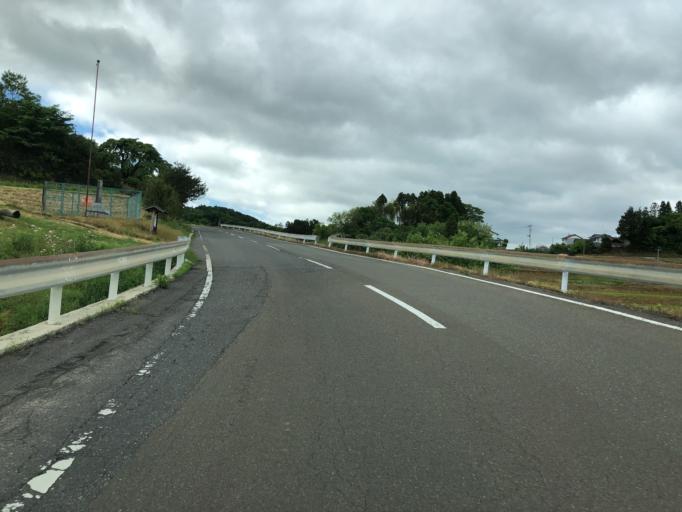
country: JP
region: Fukushima
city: Miharu
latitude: 37.4863
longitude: 140.4632
